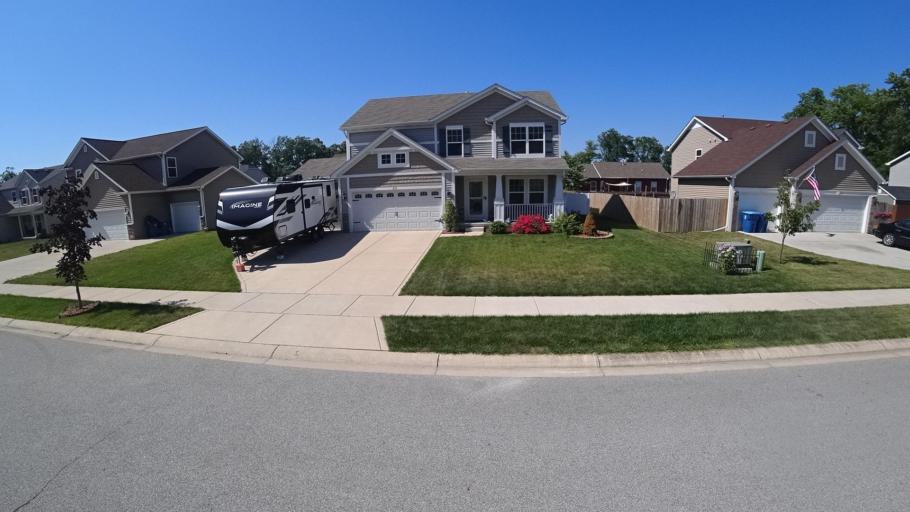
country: US
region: Indiana
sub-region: Porter County
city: Burns Harbor
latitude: 41.5998
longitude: -87.1086
